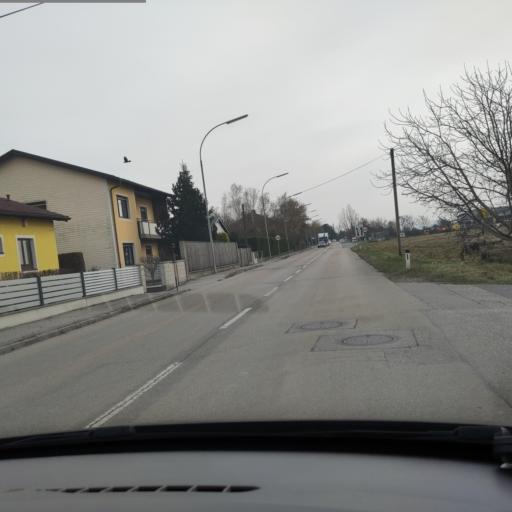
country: AT
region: Lower Austria
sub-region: Sankt Polten Stadt
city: Sankt Poelten
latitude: 48.2176
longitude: 15.6041
